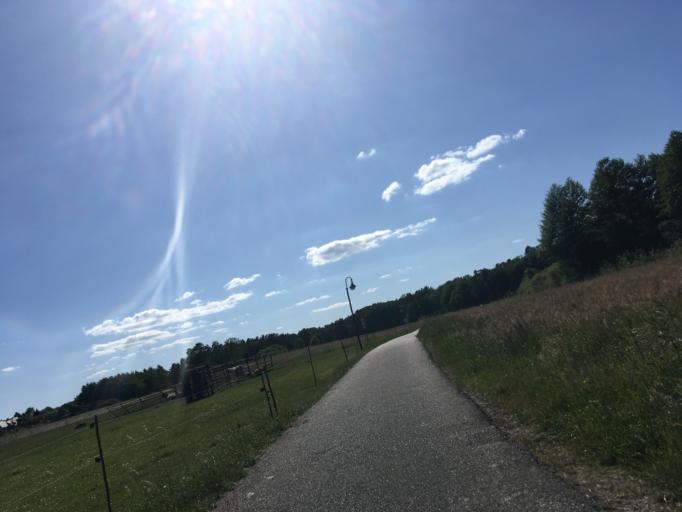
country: DE
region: Brandenburg
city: Althuttendorf
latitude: 52.9620
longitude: 13.8022
